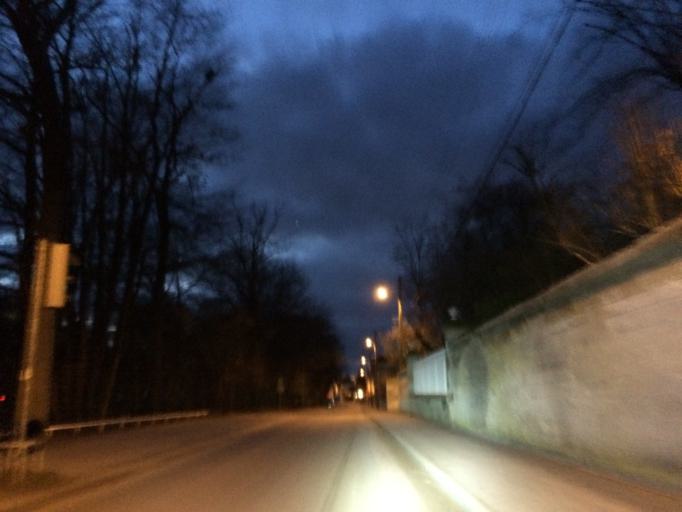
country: FR
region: Picardie
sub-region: Departement de l'Oise
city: Lamorlaye
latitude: 49.1542
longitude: 2.4498
